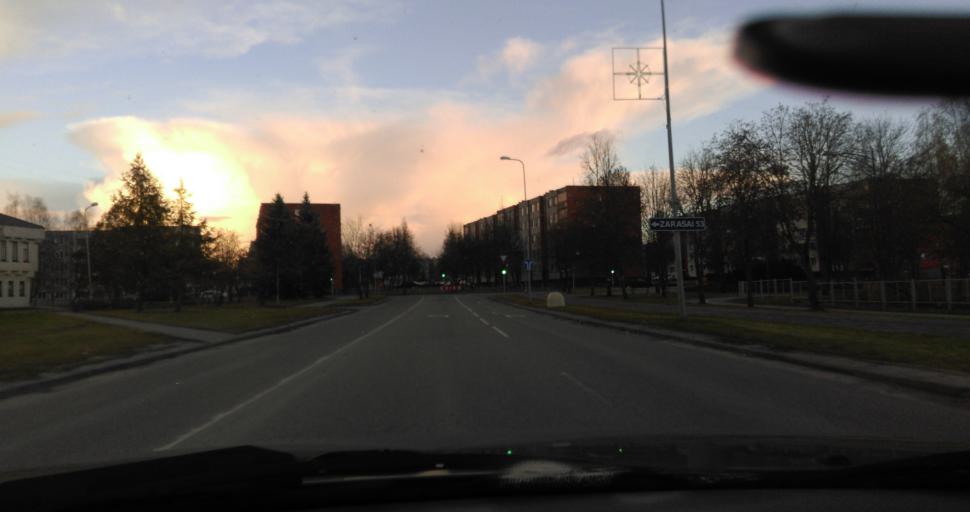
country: LT
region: Utenos apskritis
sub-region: Utena
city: Utena
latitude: 55.5098
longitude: 25.5965
